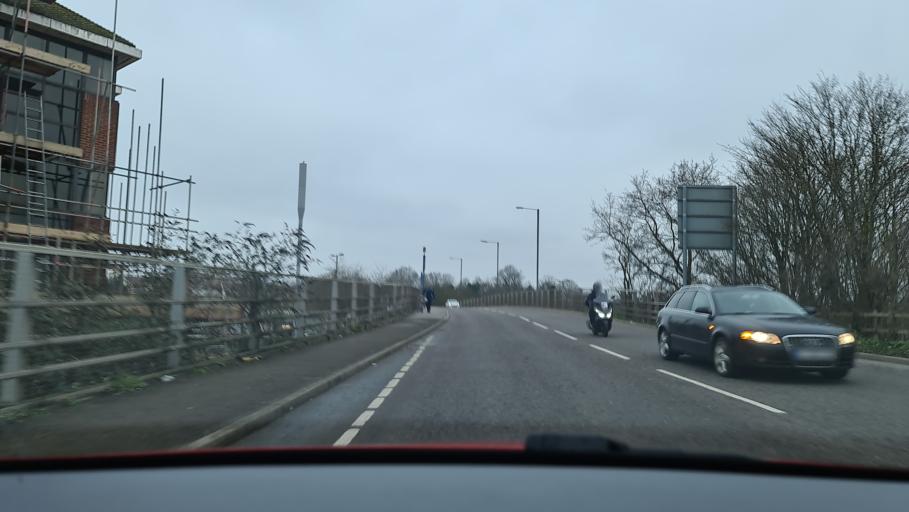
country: GB
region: England
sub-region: Greater London
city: New Malden
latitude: 51.4149
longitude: -0.2495
